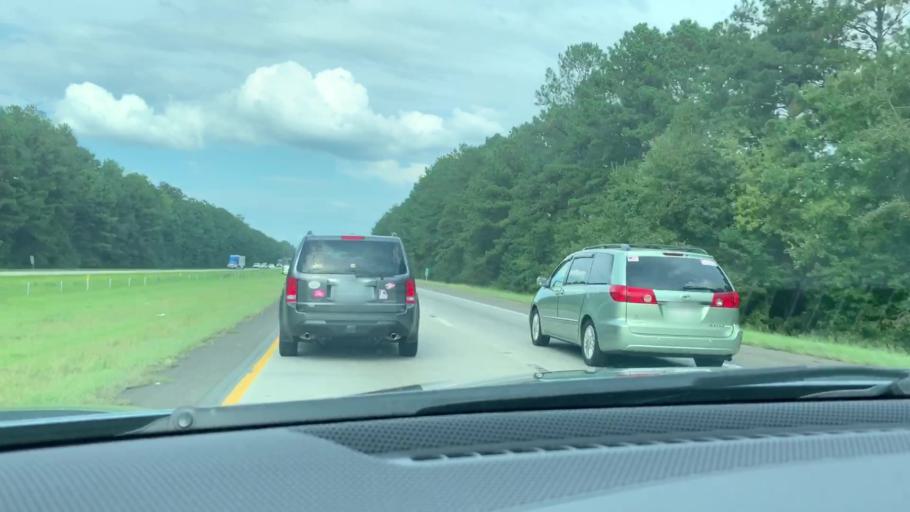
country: US
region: South Carolina
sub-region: Colleton County
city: Walterboro
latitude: 32.8337
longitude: -80.7444
